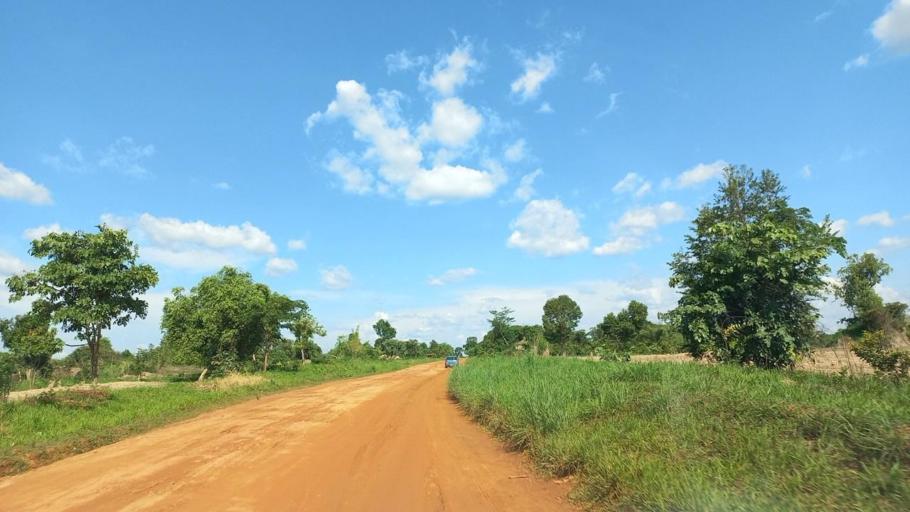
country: ZM
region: Copperbelt
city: Kitwe
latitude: -12.8705
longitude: 28.3466
